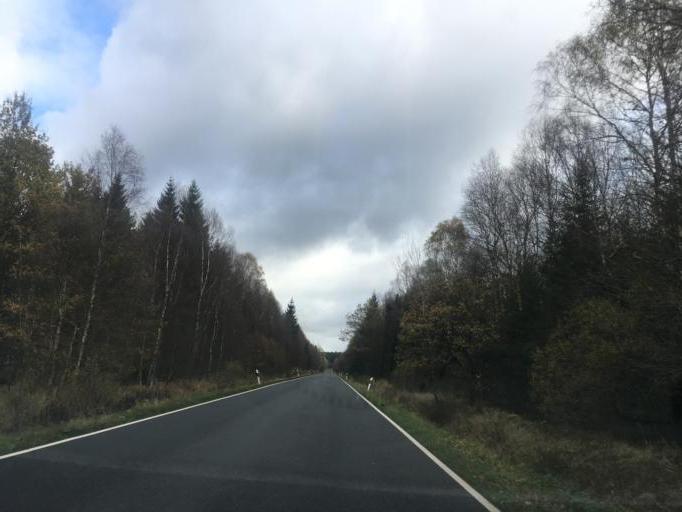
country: DE
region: Lower Saxony
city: Derental
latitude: 51.7533
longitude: 9.4791
